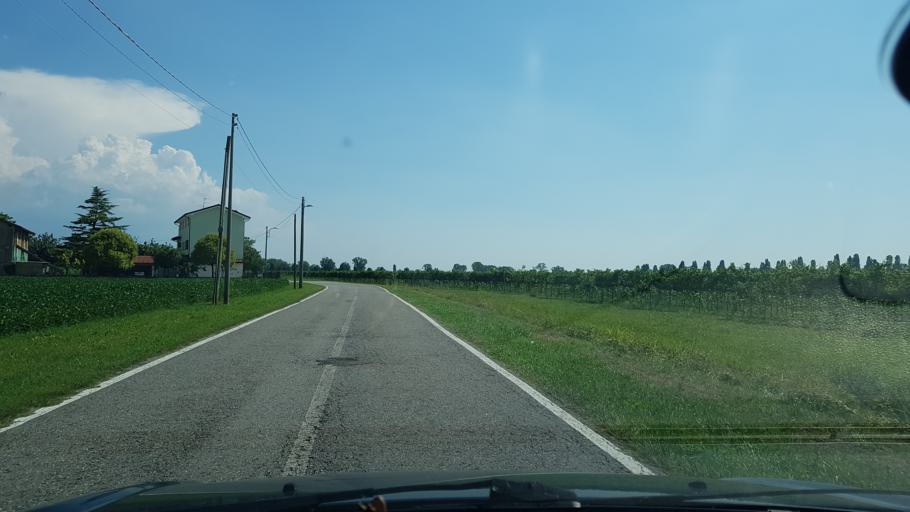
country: IT
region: Friuli Venezia Giulia
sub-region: Provincia di Gorizia
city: Staranzano
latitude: 45.7861
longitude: 13.5076
